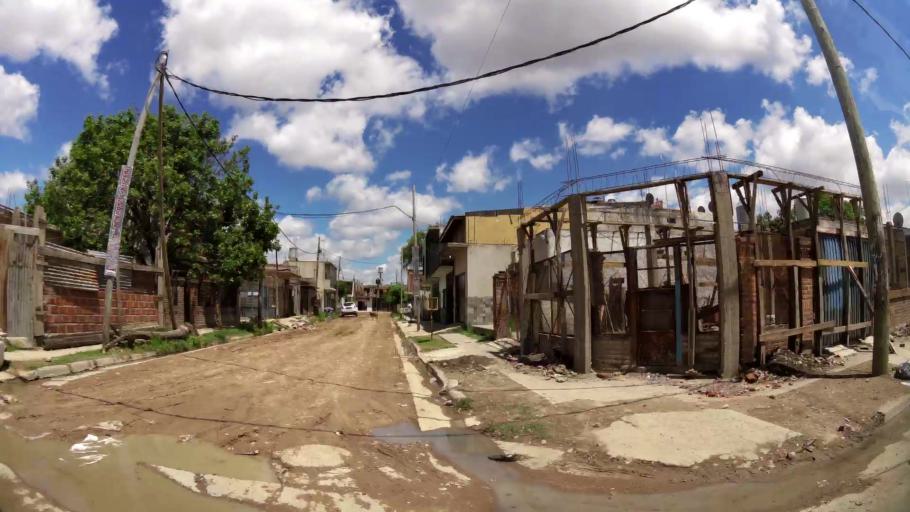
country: AR
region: Buenos Aires F.D.
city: Villa Lugano
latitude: -34.6930
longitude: -58.4439
